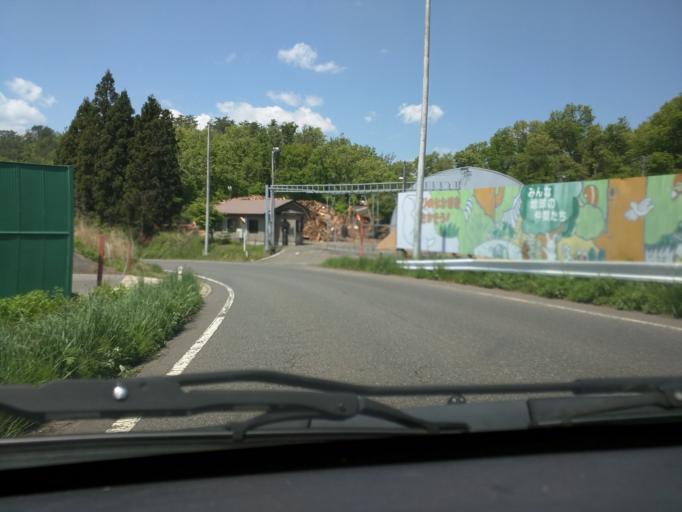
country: JP
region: Fukushima
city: Kitakata
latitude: 37.6382
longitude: 139.8170
